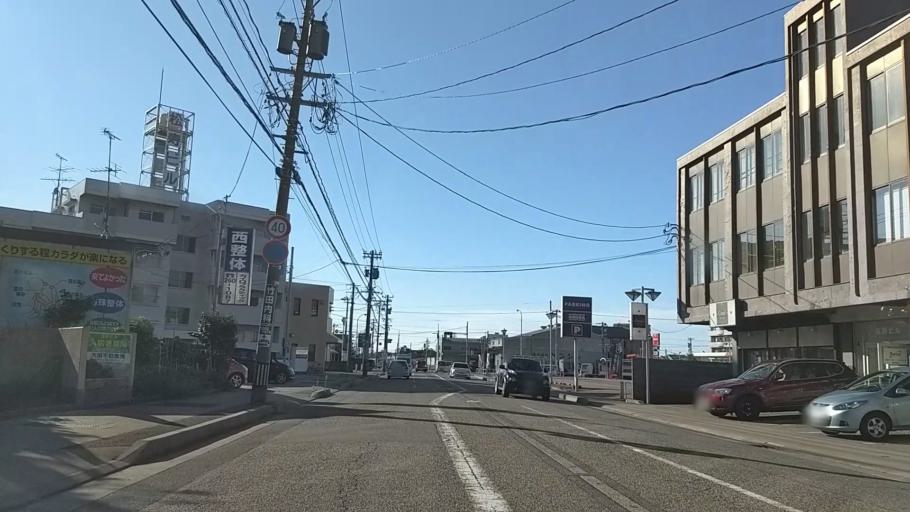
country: JP
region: Ishikawa
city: Kanazawa-shi
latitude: 36.5716
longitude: 136.6403
